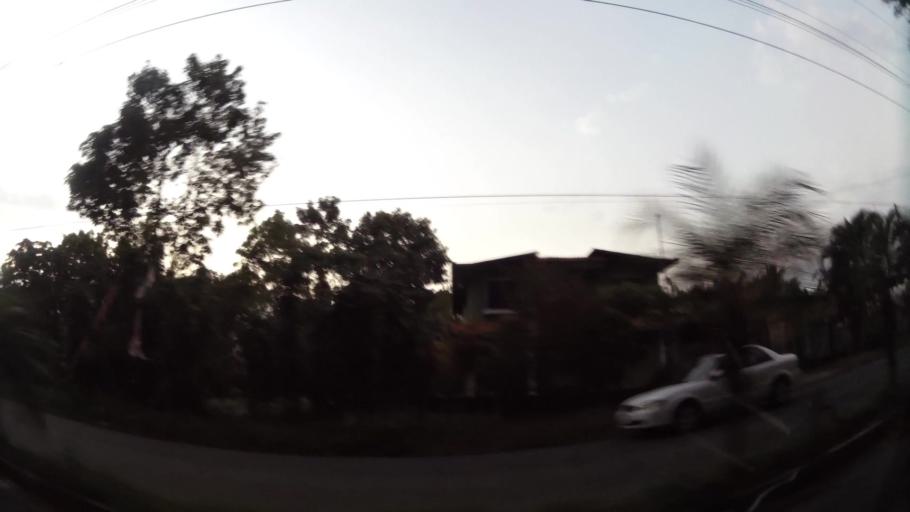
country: GT
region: Retalhuleu
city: San Felipe
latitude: 14.6199
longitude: -91.5972
